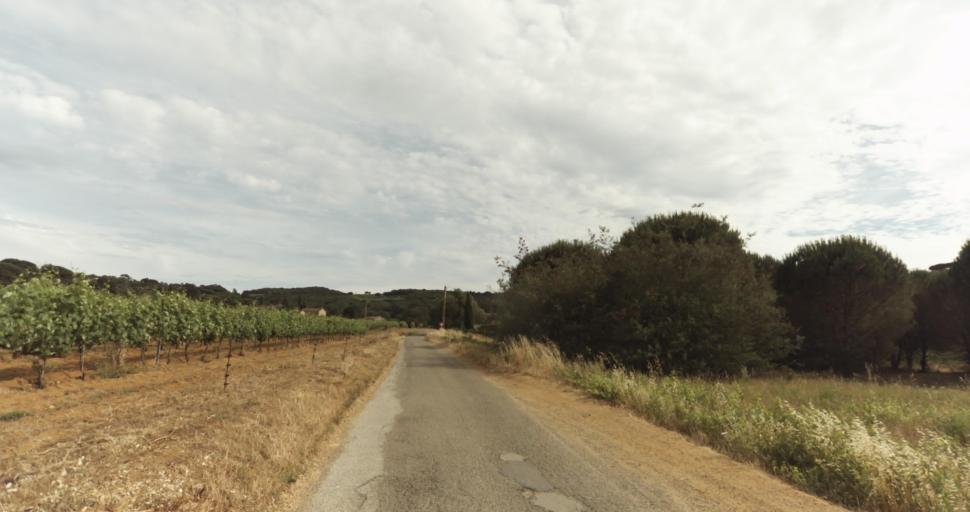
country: FR
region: Provence-Alpes-Cote d'Azur
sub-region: Departement du Var
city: Gassin
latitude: 43.2167
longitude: 6.5801
